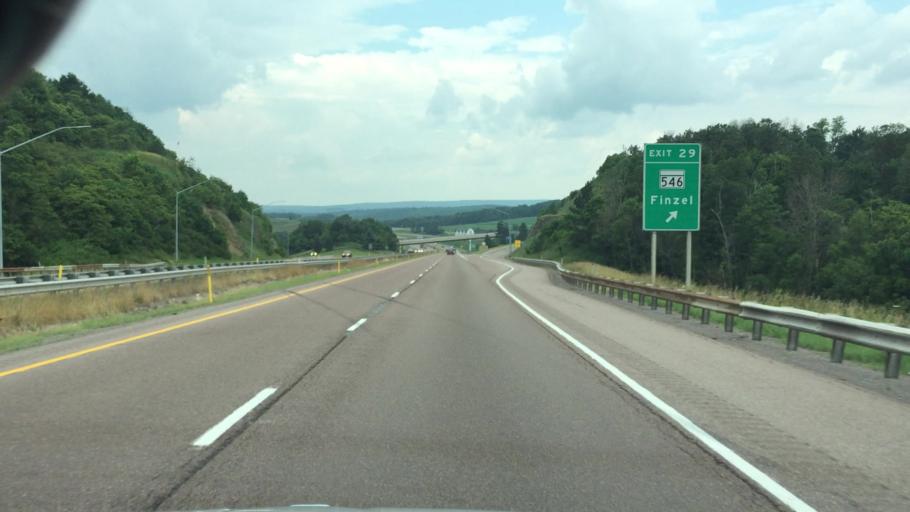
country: US
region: Maryland
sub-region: Allegany County
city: Frostburg
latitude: 39.6793
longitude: -78.9663
